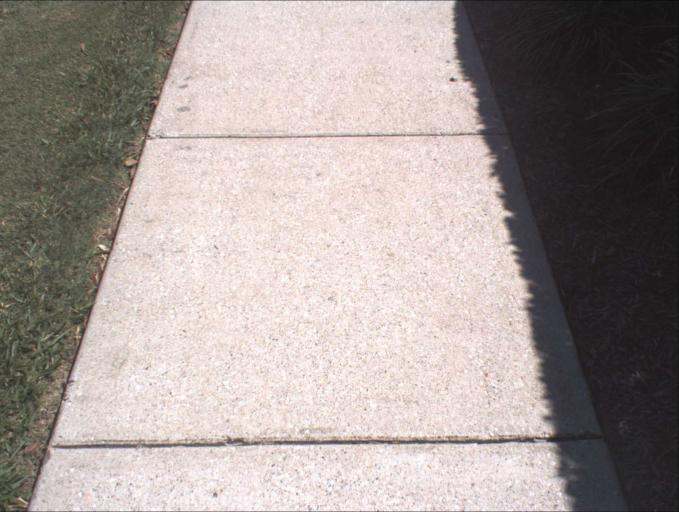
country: AU
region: Queensland
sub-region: Logan
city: Beenleigh
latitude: -27.6900
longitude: 153.2153
